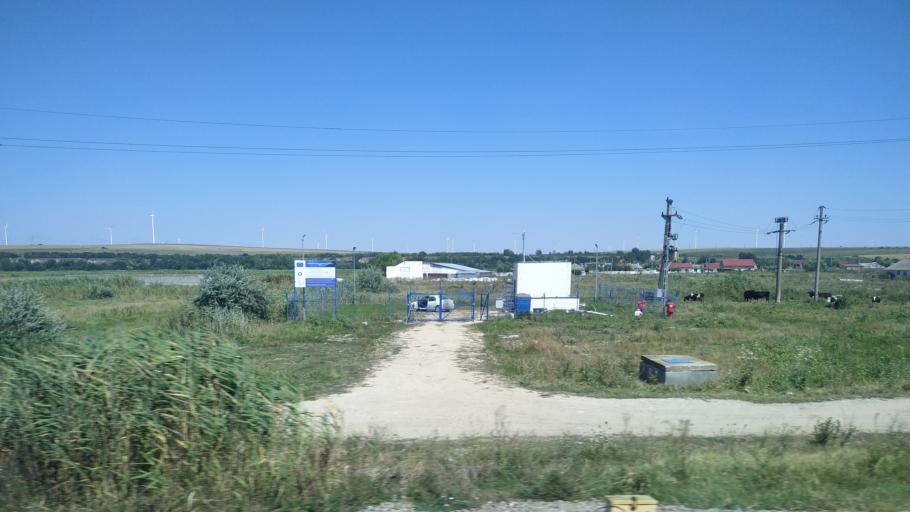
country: RO
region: Constanta
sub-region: Comuna Saligny
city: Faclia
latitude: 44.2676
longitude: 28.1344
